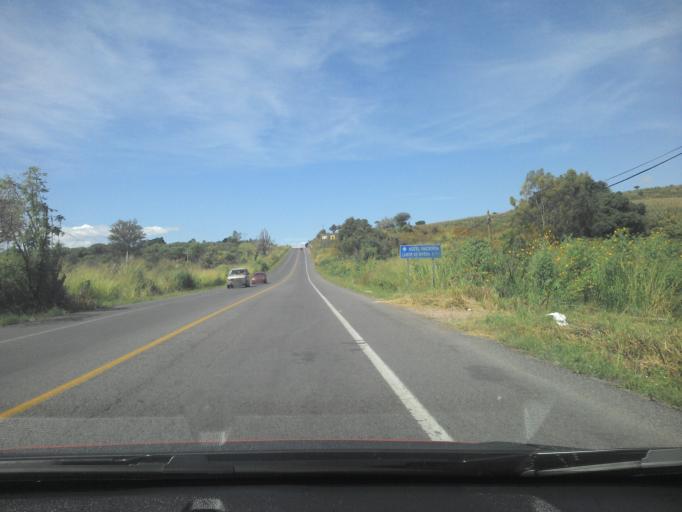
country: MX
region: Jalisco
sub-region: Teuchitlan
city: La Estanzuela
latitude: 20.6753
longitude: -103.8325
